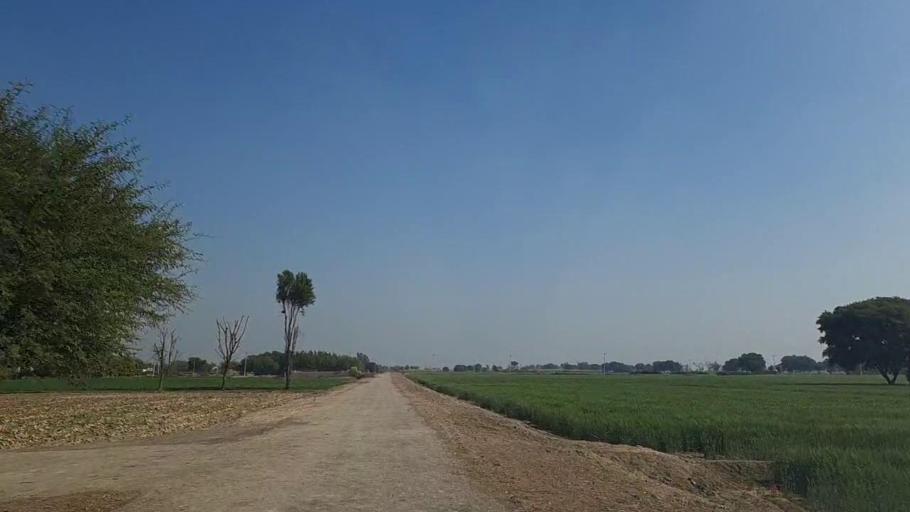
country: PK
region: Sindh
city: Shahpur Chakar
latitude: 26.2027
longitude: 68.5709
